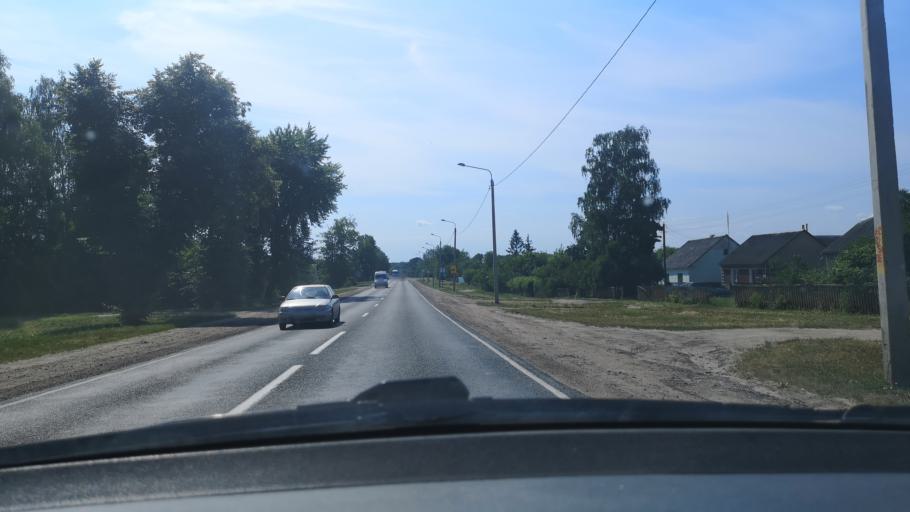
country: BY
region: Brest
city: Brest
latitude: 52.1599
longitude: 23.6675
